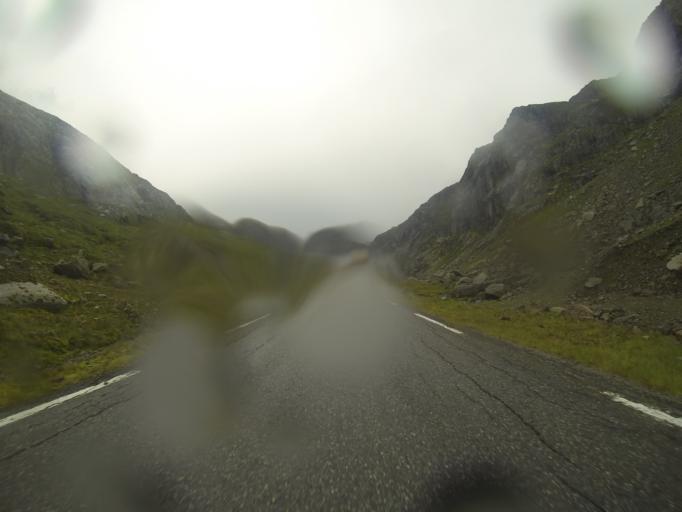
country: NO
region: Hordaland
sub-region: Odda
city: Odda
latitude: 59.7706
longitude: 6.7417
